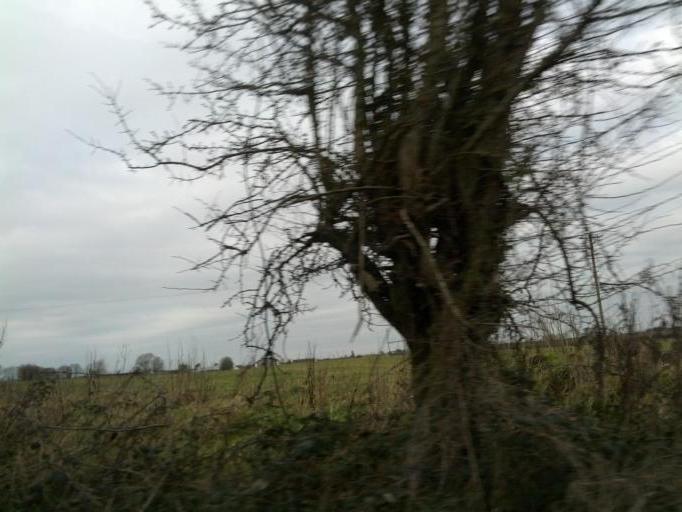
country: IE
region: Connaught
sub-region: County Galway
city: Oranmore
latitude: 53.2073
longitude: -8.8932
